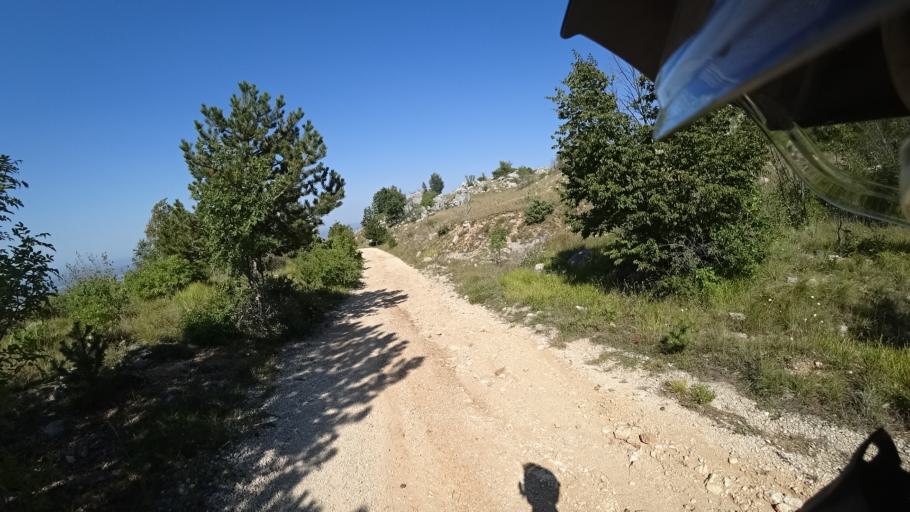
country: HR
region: Sibensko-Kniniska
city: Drnis
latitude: 43.9197
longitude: 16.1689
